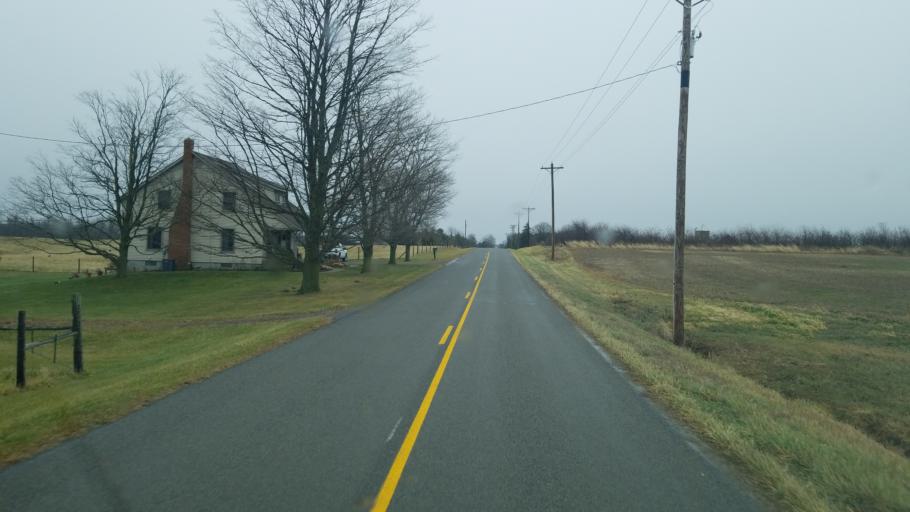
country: US
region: Ohio
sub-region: Logan County
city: Northwood
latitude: 40.4471
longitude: -83.6220
